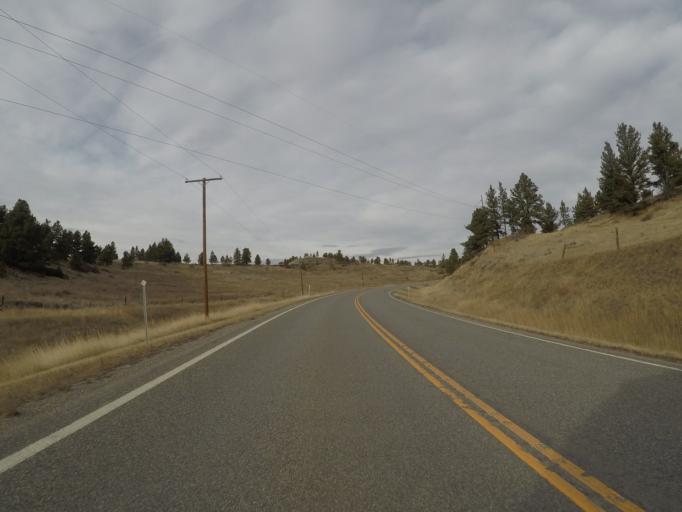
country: US
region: Montana
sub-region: Yellowstone County
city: Laurel
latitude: 45.8320
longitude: -108.7233
